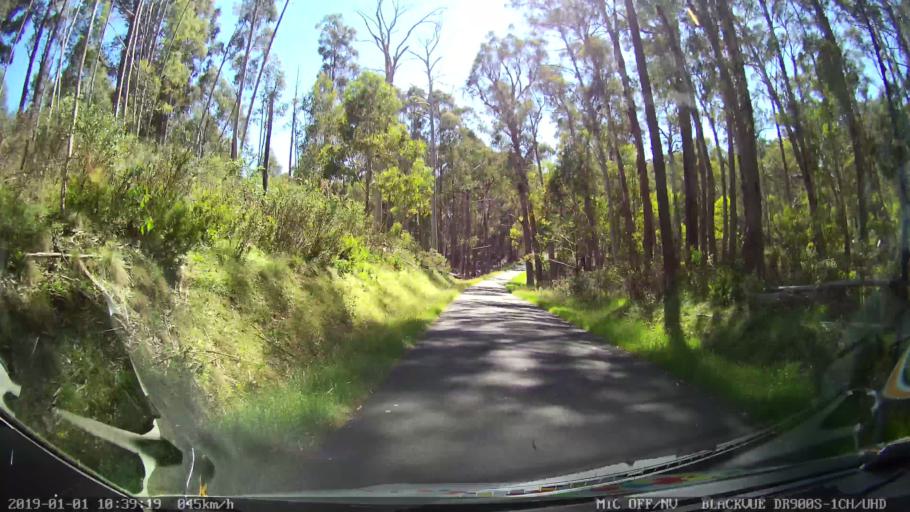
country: AU
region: New South Wales
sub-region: Snowy River
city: Jindabyne
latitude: -36.0407
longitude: 148.3033
